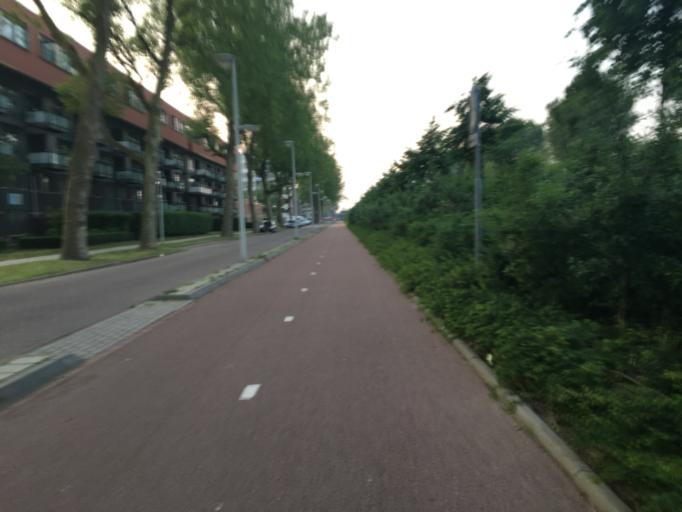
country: NL
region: South Holland
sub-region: Gemeente Schiedam
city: Schiedam
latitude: 51.9302
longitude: 4.3751
